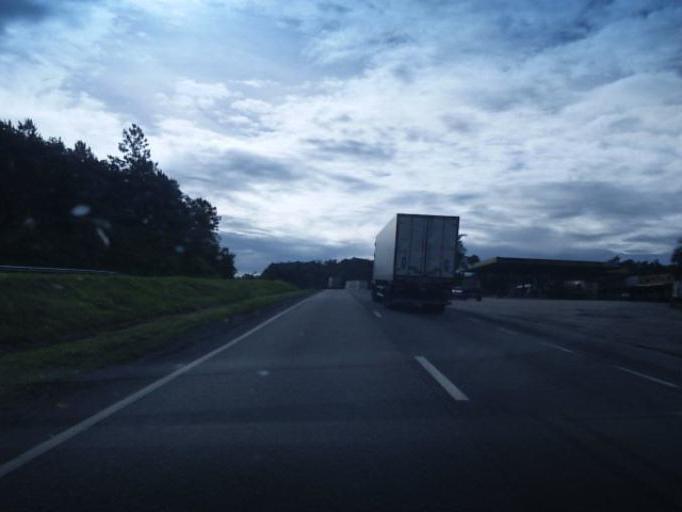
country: BR
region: Parana
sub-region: Antonina
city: Antonina
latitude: -25.1033
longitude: -48.7045
